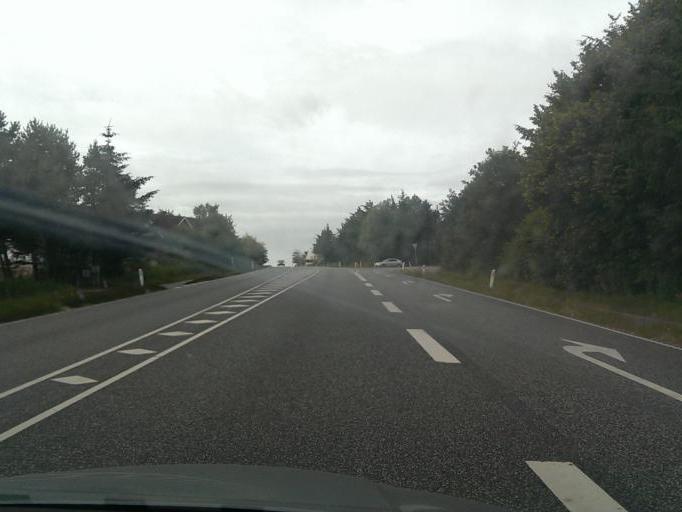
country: DK
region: North Denmark
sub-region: Hjorring Kommune
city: Hjorring
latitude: 57.4532
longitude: 9.9204
